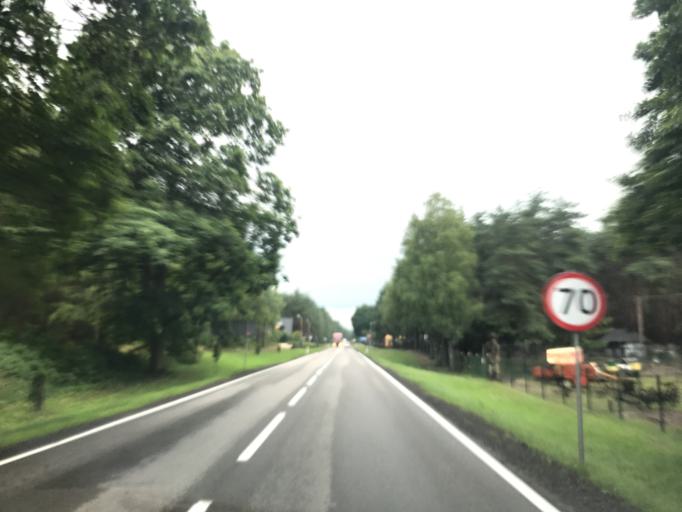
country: PL
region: Pomeranian Voivodeship
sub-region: Powiat czluchowski
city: Rzeczenica
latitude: 53.8043
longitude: 17.0179
